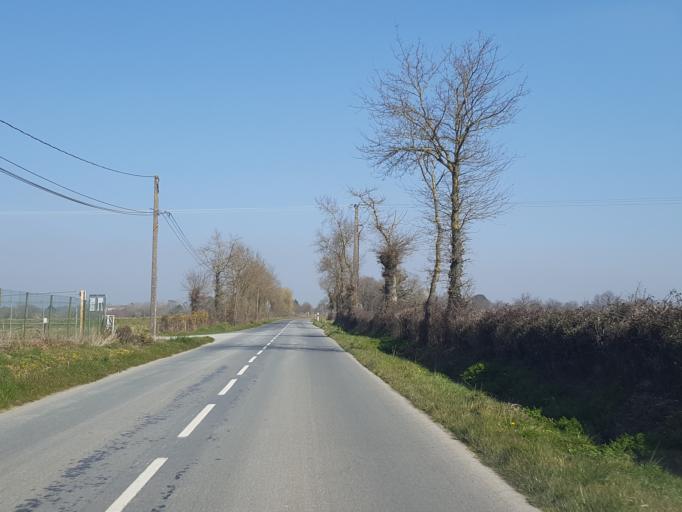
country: FR
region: Pays de la Loire
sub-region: Departement de la Vendee
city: La Chaize-le-Vicomte
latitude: 46.6623
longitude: -1.2970
